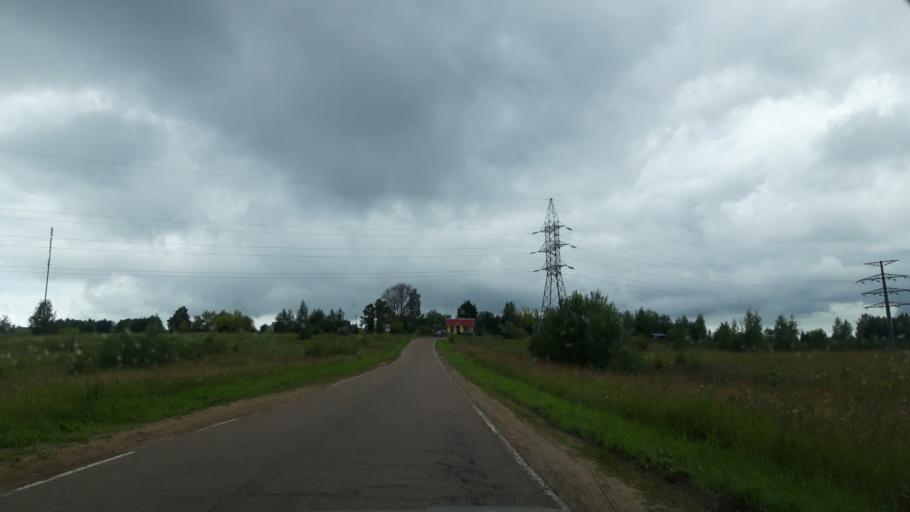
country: RU
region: Moskovskaya
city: Lozhki
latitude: 56.0909
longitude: 37.0757
